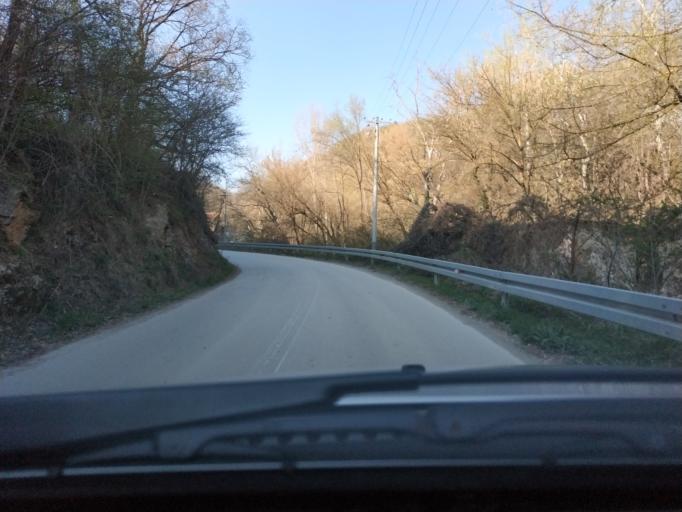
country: RS
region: Central Serbia
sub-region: Nisavski Okrug
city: Aleksinac
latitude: 43.5356
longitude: 21.8042
